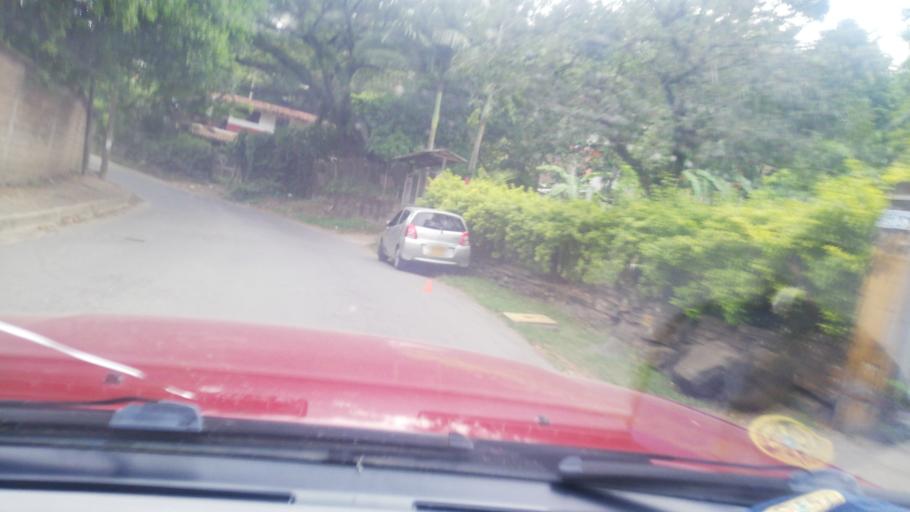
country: CO
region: Valle del Cauca
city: Cali
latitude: 3.4766
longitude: -76.5541
